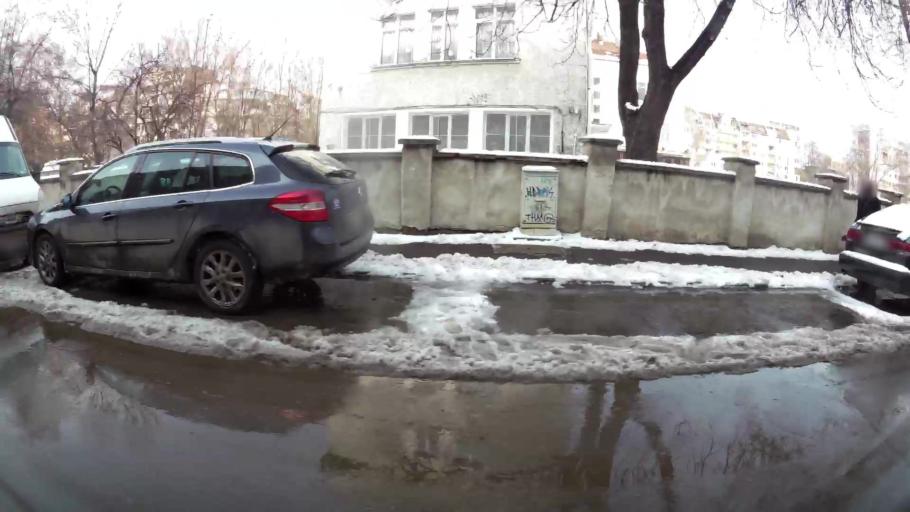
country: BG
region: Sofia-Capital
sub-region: Stolichna Obshtina
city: Sofia
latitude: 42.7057
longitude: 23.3531
